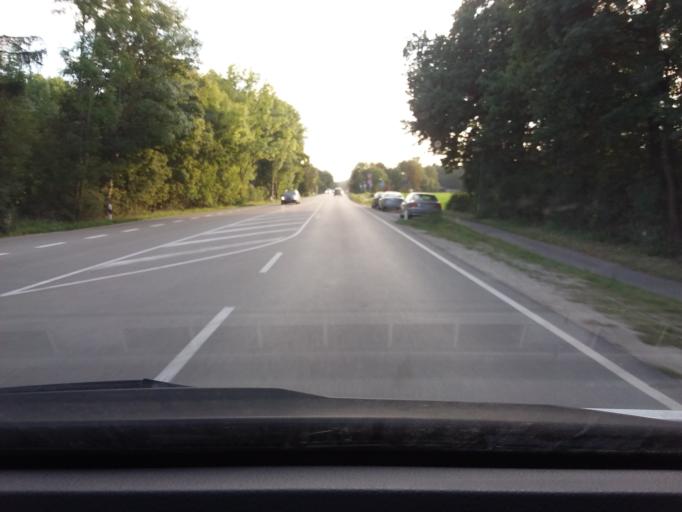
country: DE
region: Bavaria
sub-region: Upper Bavaria
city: Oberschleissheim
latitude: 48.2582
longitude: 11.5867
